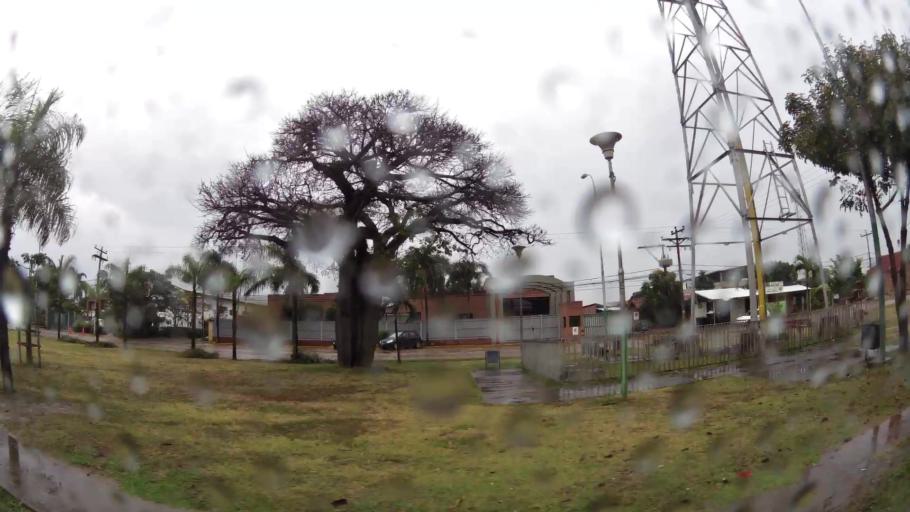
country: BO
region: Santa Cruz
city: Santa Cruz de la Sierra
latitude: -17.8163
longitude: -63.2247
